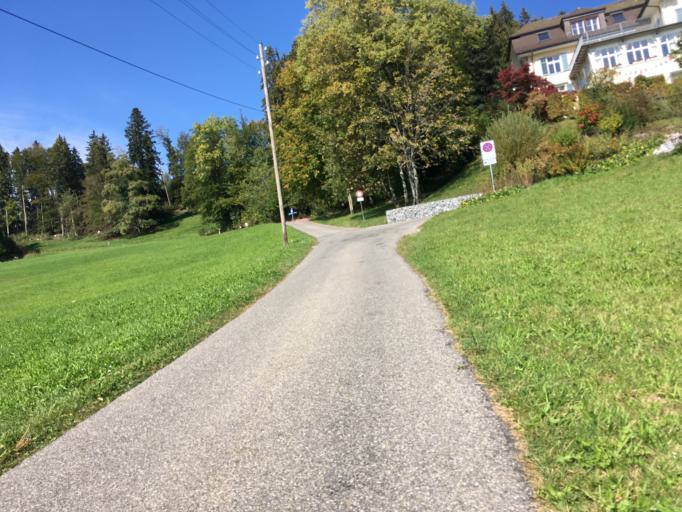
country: CH
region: Zurich
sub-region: Bezirk Hinwil
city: Baretswil
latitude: 47.3451
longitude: 8.8430
